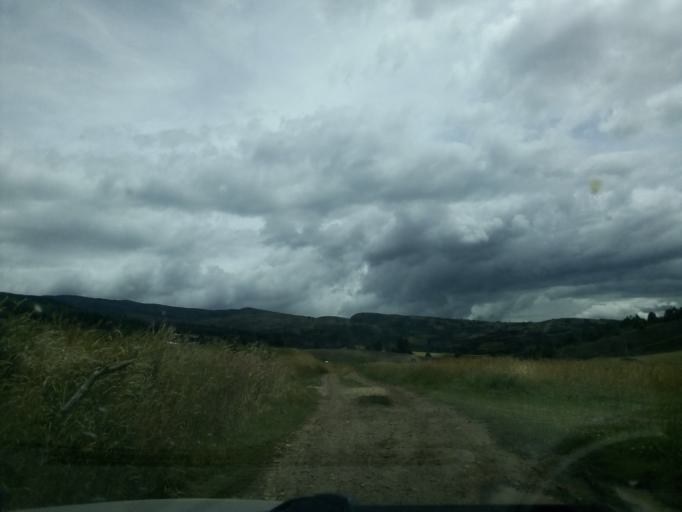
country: CO
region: Boyaca
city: Toca
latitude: 5.6025
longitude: -73.1133
